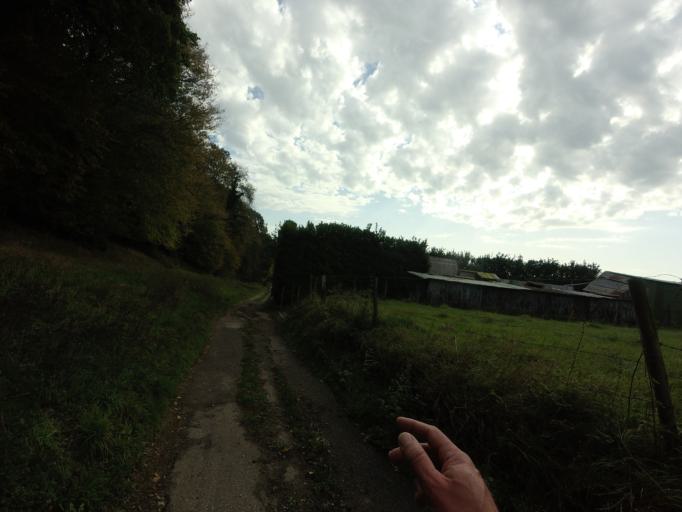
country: NL
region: Limburg
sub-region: Valkenburg aan de Geul
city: Schin op Geul
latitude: 50.7899
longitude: 5.8995
